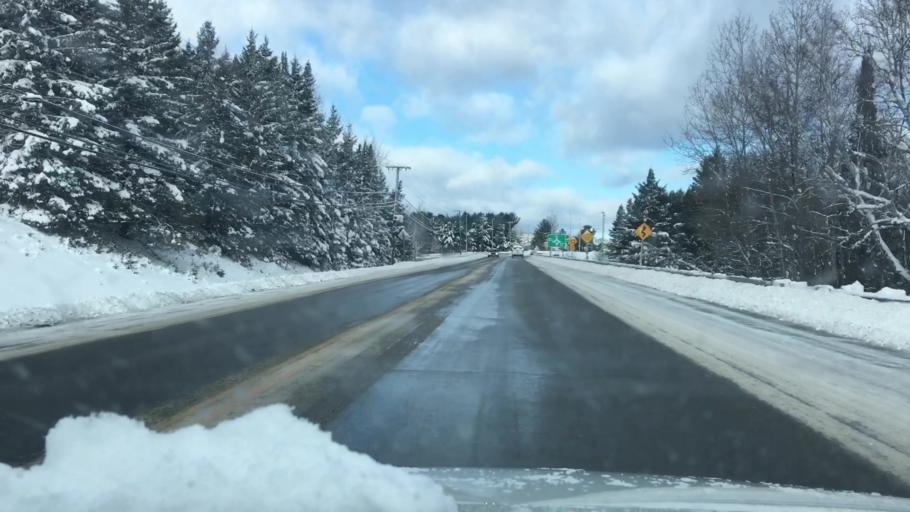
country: US
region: Maine
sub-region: Aroostook County
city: Caribou
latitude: 46.8768
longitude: -68.0077
